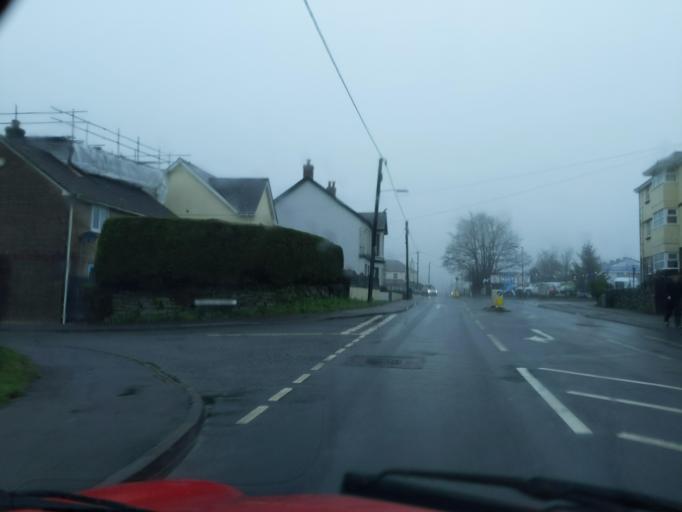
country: GB
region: England
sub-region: Cornwall
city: Callington
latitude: 50.5197
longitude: -4.3159
